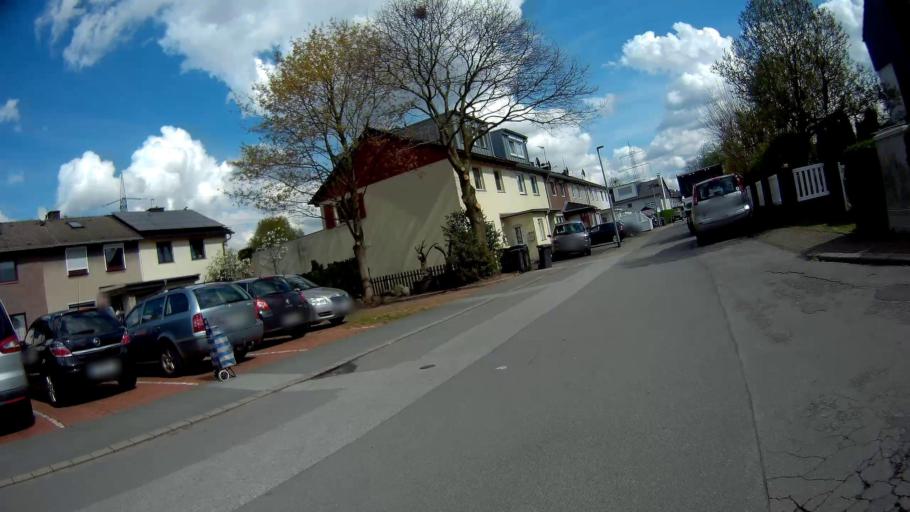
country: DE
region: North Rhine-Westphalia
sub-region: Regierungsbezirk Munster
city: Gladbeck
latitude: 51.5547
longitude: 7.0207
